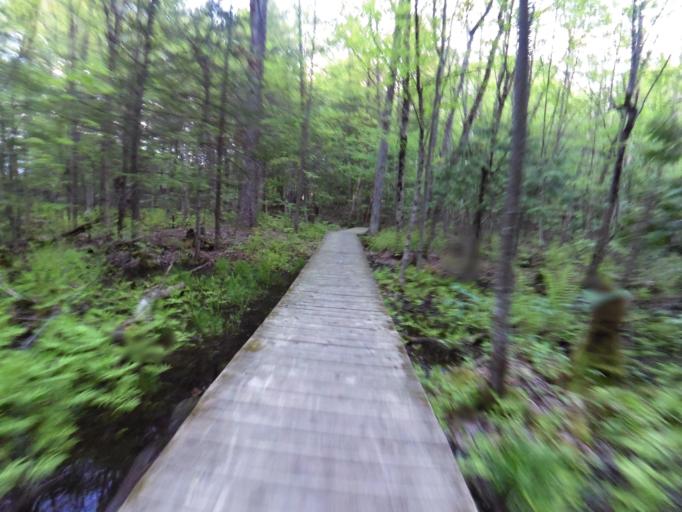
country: CA
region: Ontario
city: Bells Corners
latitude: 45.3237
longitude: -75.8115
